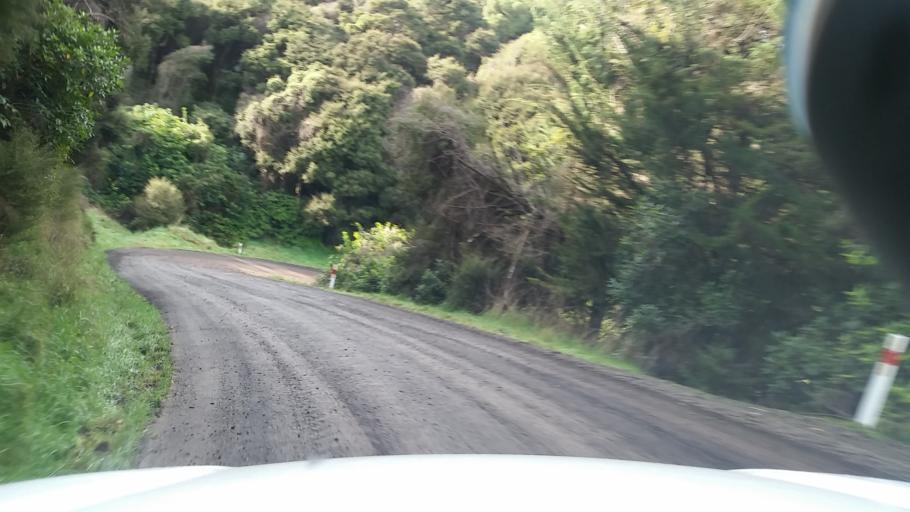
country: NZ
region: Canterbury
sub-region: Christchurch City
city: Christchurch
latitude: -43.6698
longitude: 172.8721
